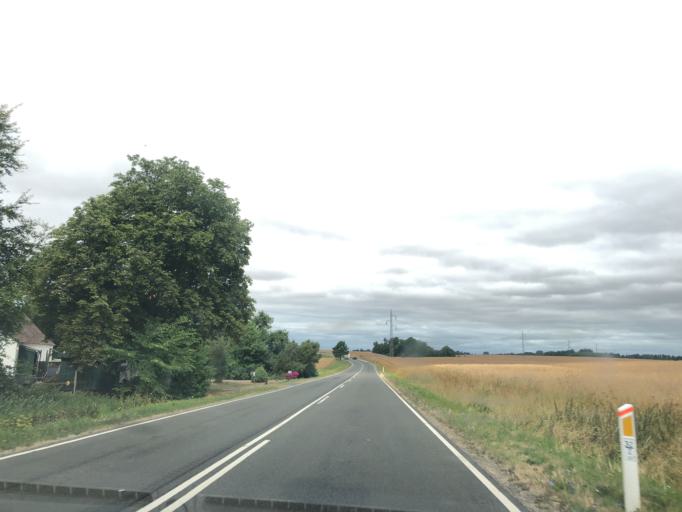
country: DK
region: Zealand
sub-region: Slagelse Kommune
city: Skaelskor
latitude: 55.2997
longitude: 11.3266
